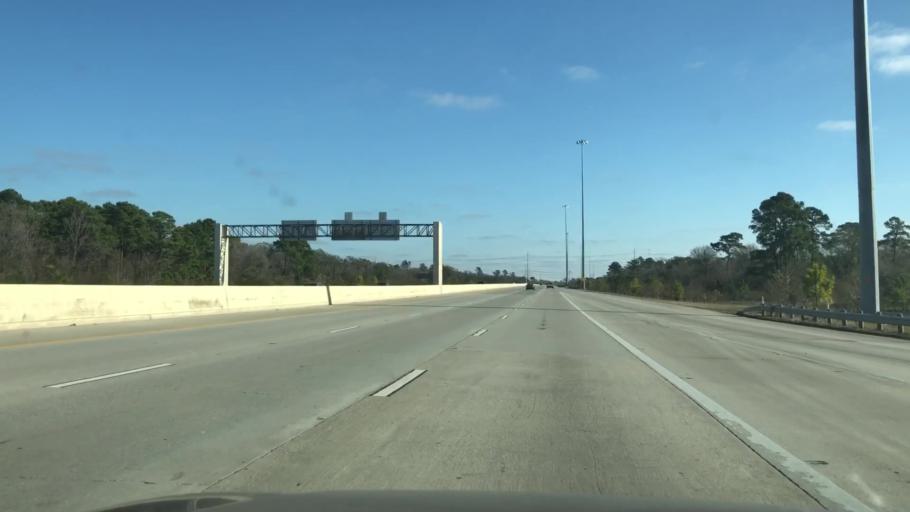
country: US
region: Texas
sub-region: Harris County
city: Jacinto City
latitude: 29.7864
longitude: -95.2434
